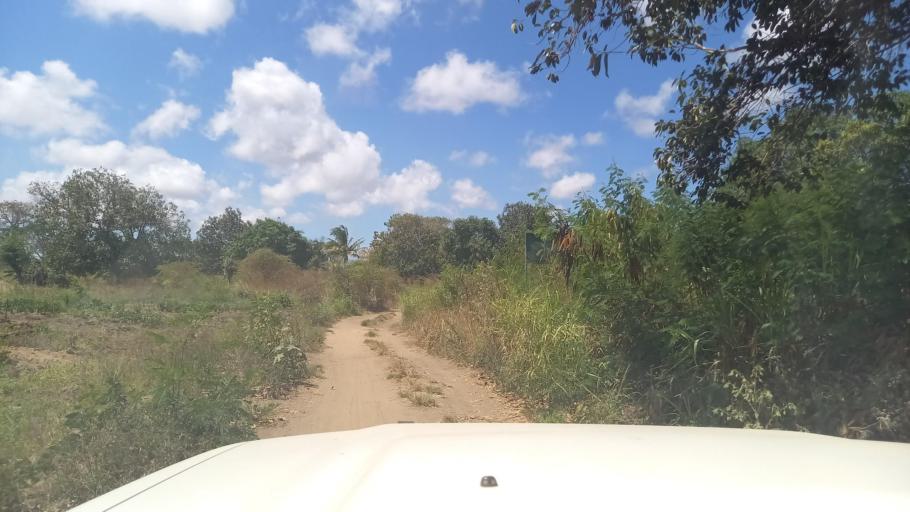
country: MZ
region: Cabo Delgado
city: Pemba
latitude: -13.4252
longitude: 40.4868
